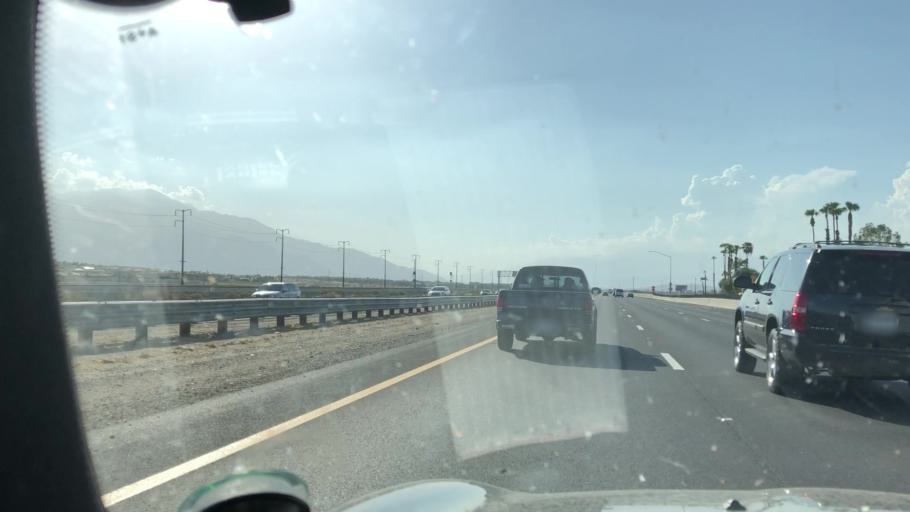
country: US
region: California
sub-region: Riverside County
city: Thousand Palms
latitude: 33.7889
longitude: -116.3593
